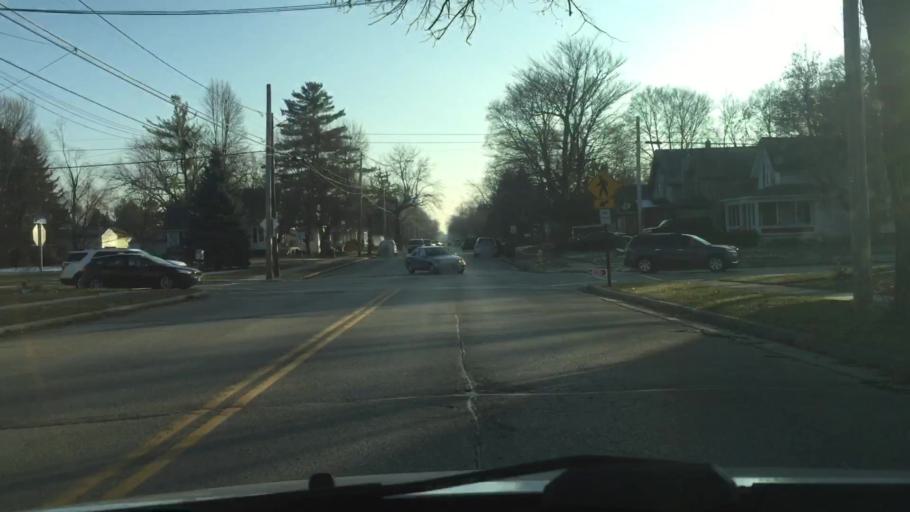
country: US
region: Wisconsin
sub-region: Waukesha County
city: Oconomowoc
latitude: 43.1054
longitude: -88.4959
